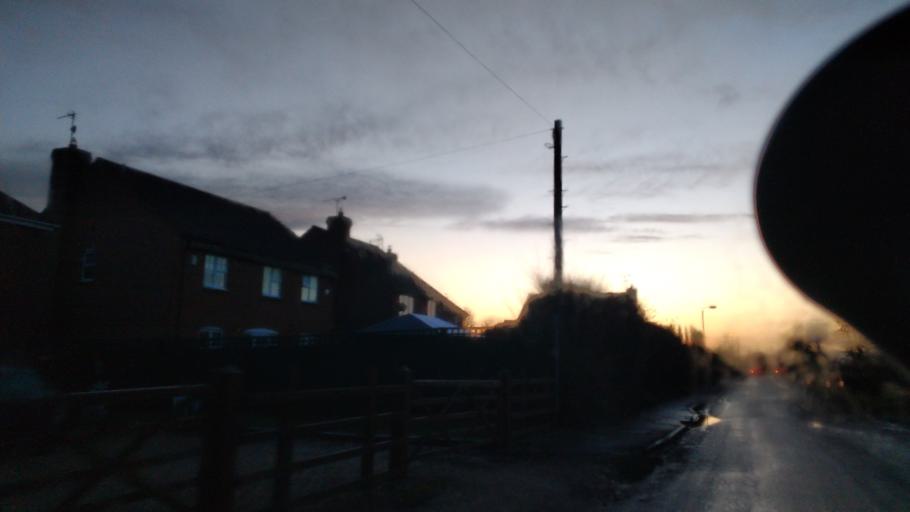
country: GB
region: England
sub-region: Borough of Swindon
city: Highworth
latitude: 51.5894
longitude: -1.7198
